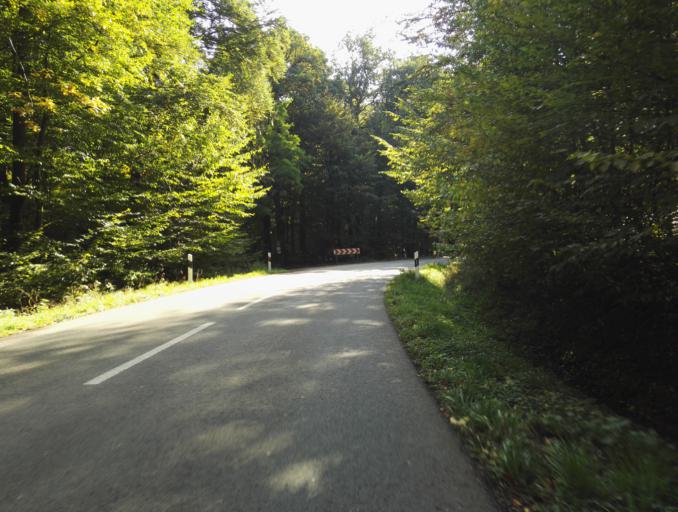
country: DE
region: Lower Saxony
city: Holle
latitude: 52.1292
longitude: 10.1397
